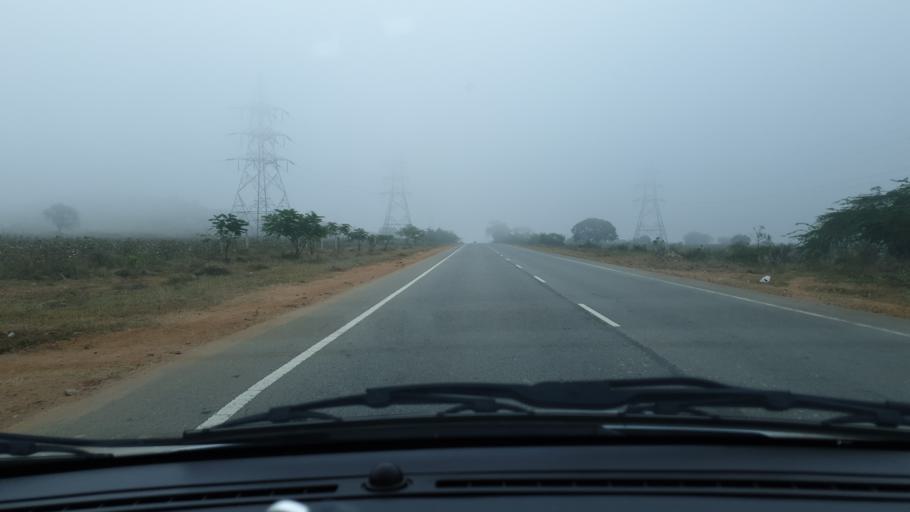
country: IN
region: Telangana
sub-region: Nalgonda
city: Devarkonda
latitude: 16.6286
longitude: 78.6633
